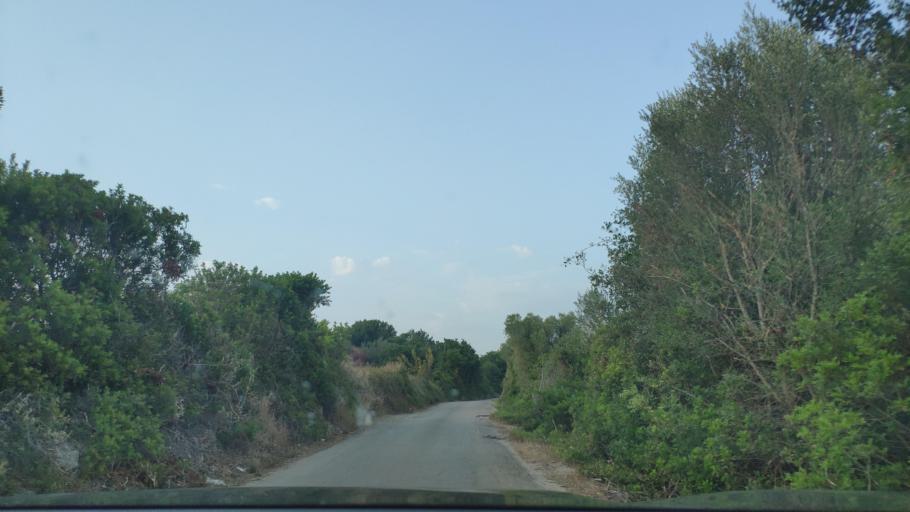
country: GR
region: West Greece
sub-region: Nomos Aitolias kai Akarnanias
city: Monastirakion
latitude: 38.9161
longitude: 20.9671
